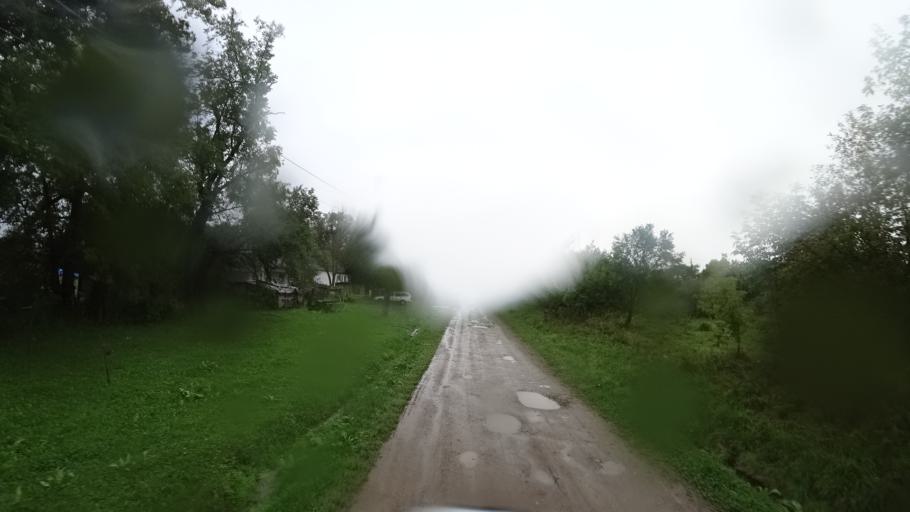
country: RU
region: Primorskiy
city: Monastyrishche
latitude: 44.2530
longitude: 132.4265
